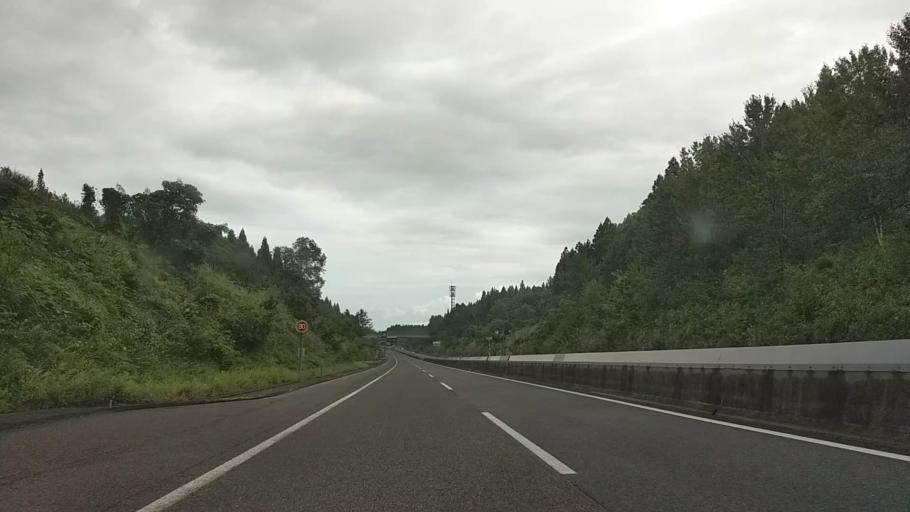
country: JP
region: Niigata
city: Arai
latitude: 36.9594
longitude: 138.2193
